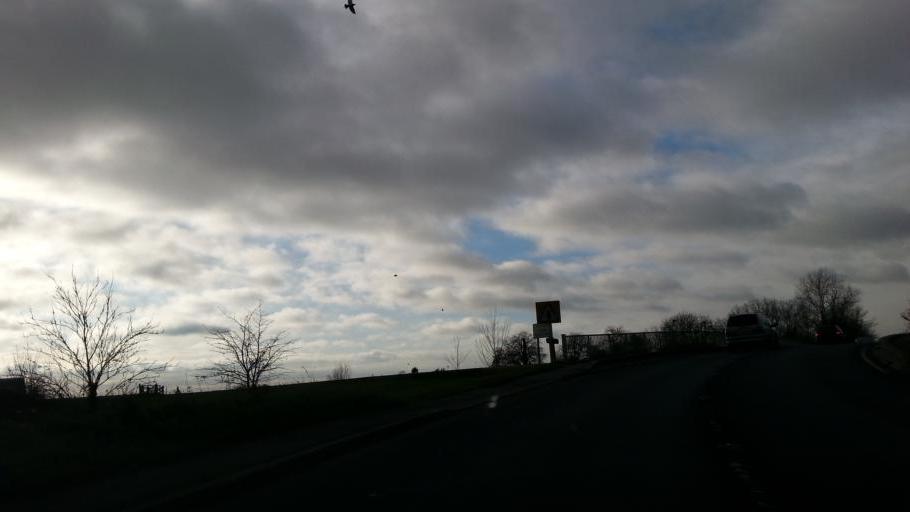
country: GB
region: England
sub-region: Norfolk
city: Downham Market
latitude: 52.6004
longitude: 0.3578
